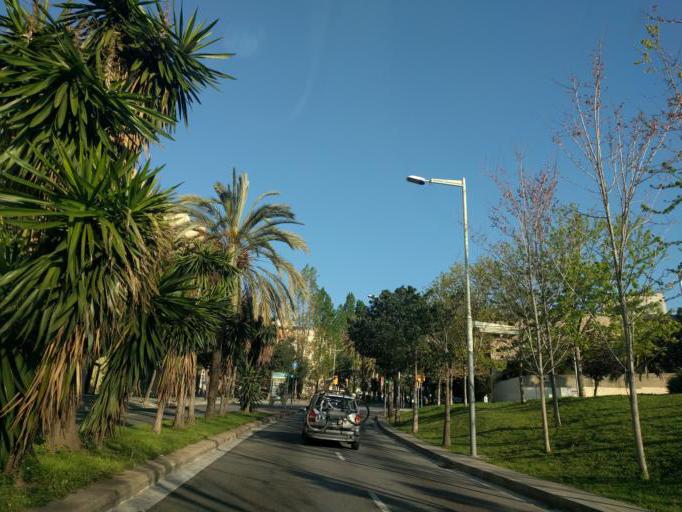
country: ES
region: Catalonia
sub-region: Provincia de Barcelona
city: Sarria-Sant Gervasi
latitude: 41.4133
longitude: 2.1412
